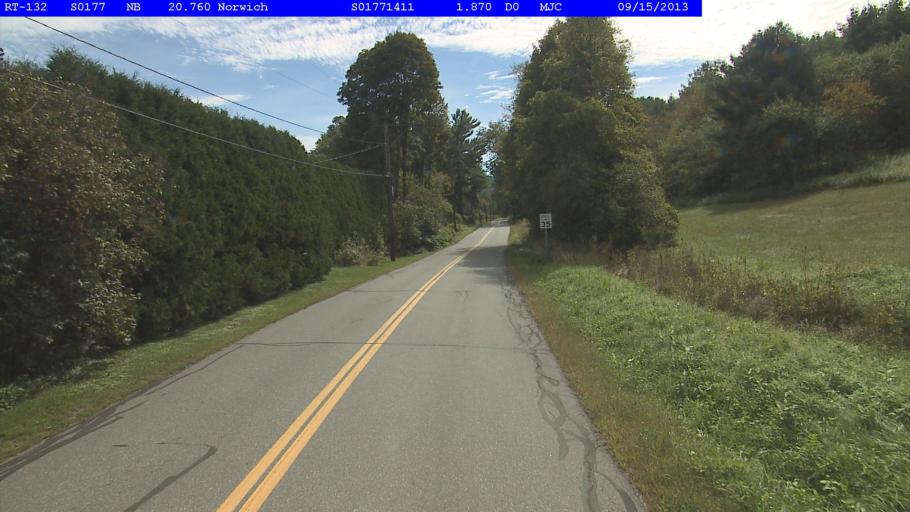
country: US
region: New Hampshire
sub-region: Grafton County
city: Hanover
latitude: 43.7651
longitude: -72.2431
